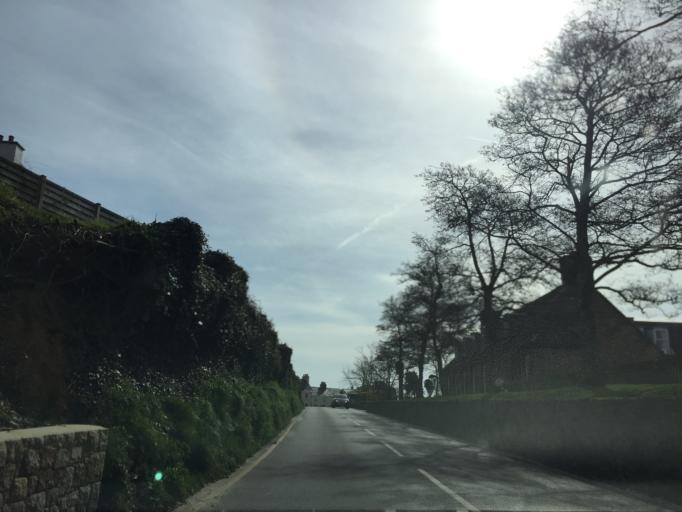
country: JE
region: St Helier
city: Saint Helier
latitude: 49.2333
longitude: -2.0910
